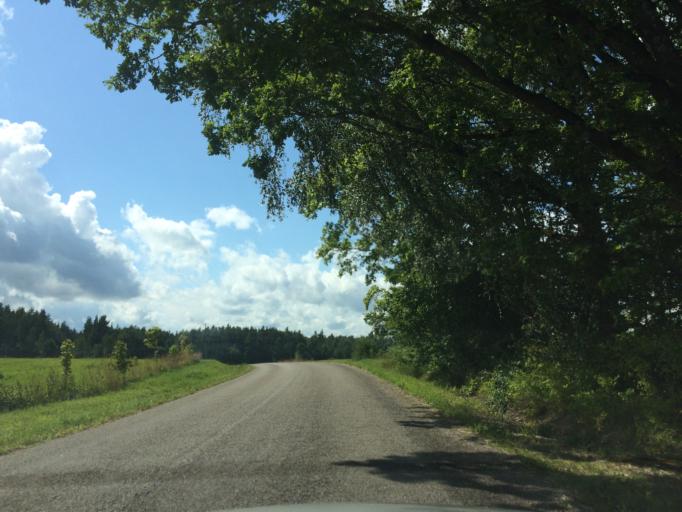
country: LV
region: Rezekne
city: Rezekne
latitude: 56.5526
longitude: 27.3718
